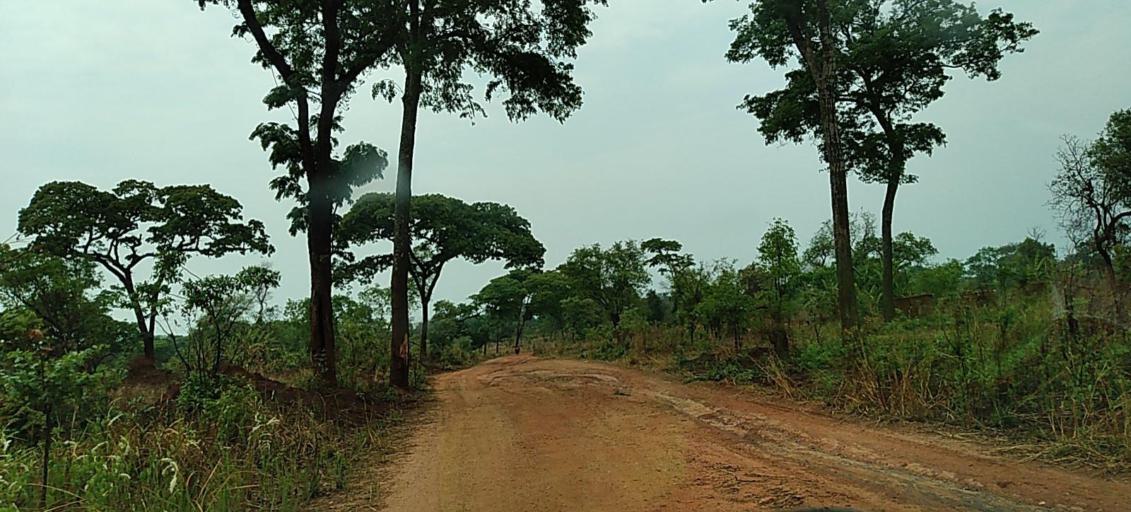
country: ZM
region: North-Western
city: Solwezi
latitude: -12.3374
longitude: 26.5241
